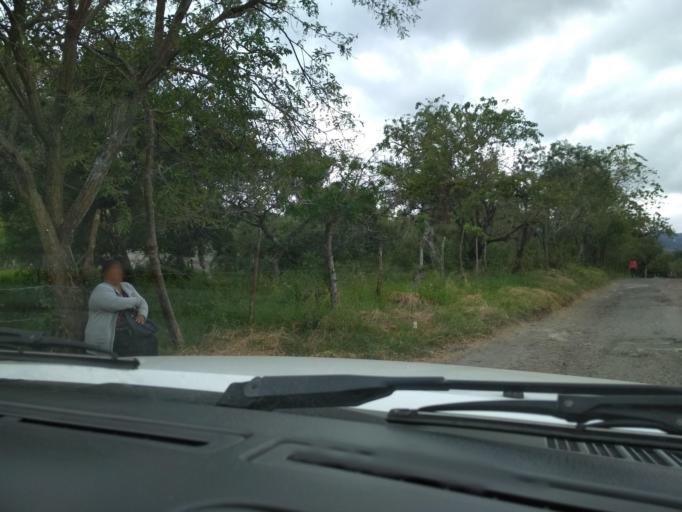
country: MX
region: Veracruz
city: El Castillo
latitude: 19.5869
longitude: -96.8324
